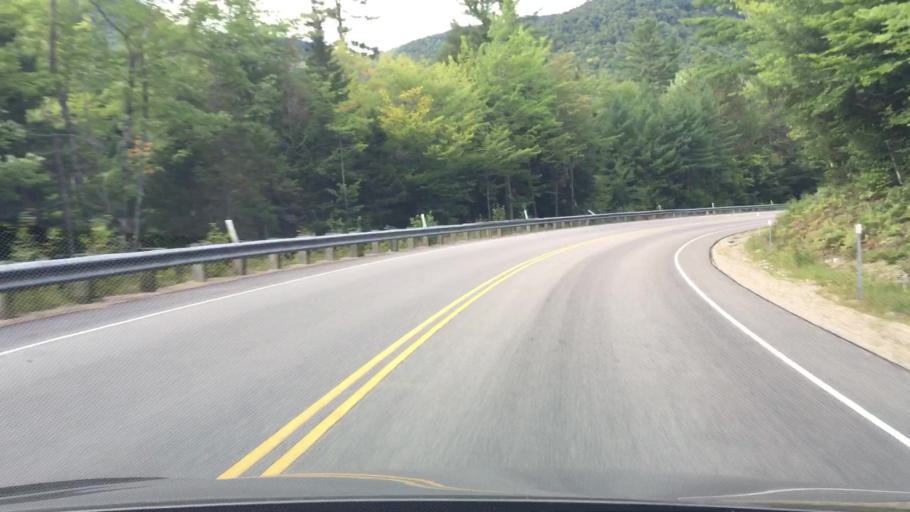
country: US
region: New Hampshire
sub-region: Carroll County
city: Tamworth
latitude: 44.0058
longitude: -71.2774
